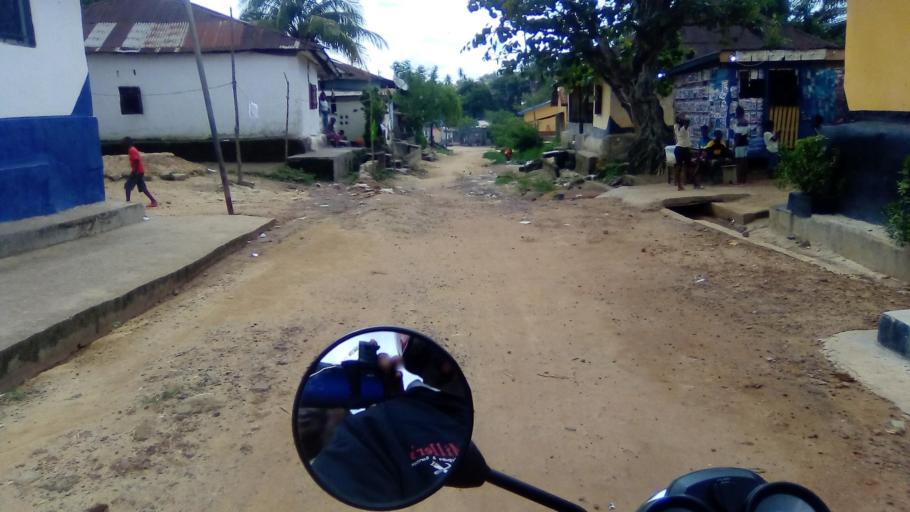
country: SL
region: Southern Province
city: Bo
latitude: 7.9632
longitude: -11.7332
